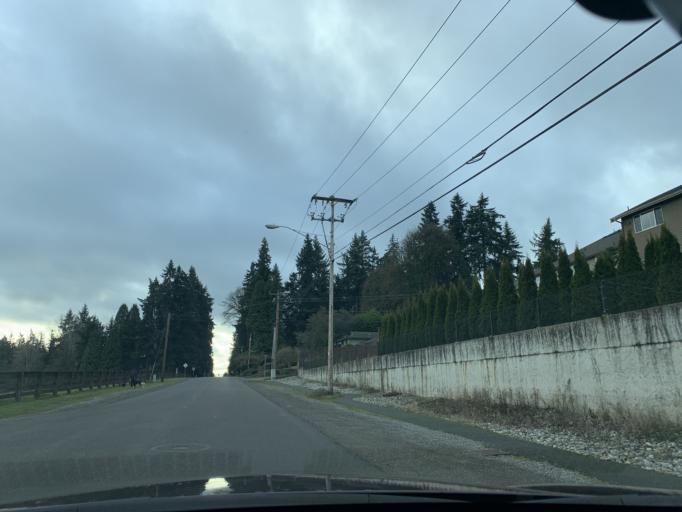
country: US
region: Washington
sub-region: King County
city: Kingsgate
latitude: 47.7329
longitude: -122.1638
